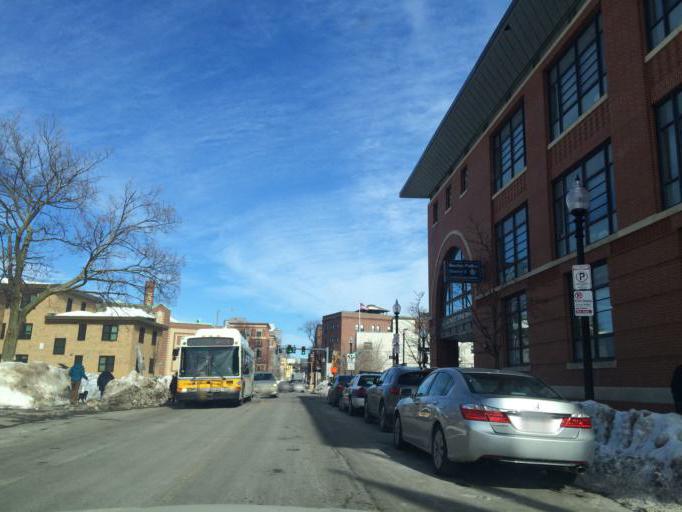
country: US
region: Massachusetts
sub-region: Suffolk County
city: South Boston
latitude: 42.3395
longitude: -71.0695
